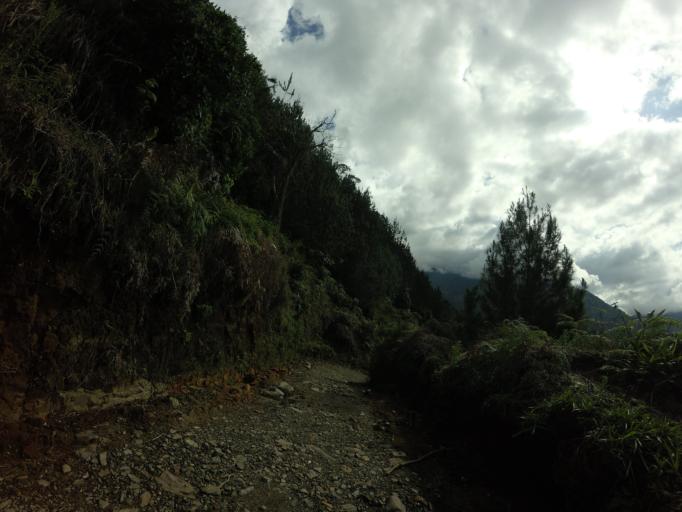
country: CO
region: Caldas
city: Pensilvania
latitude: 5.4615
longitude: -75.1683
